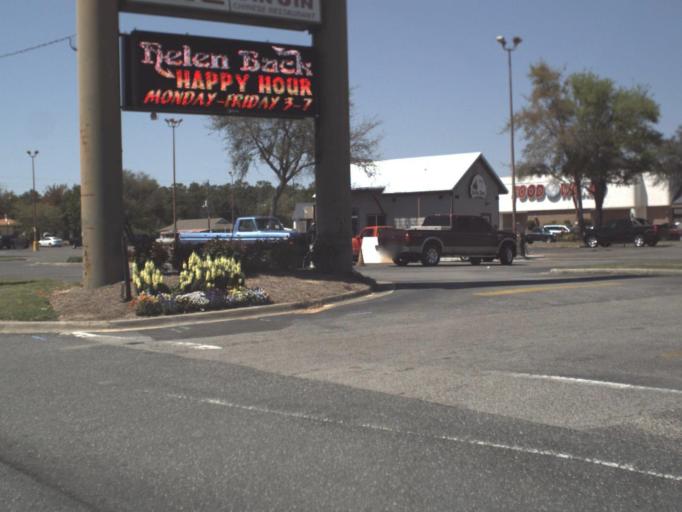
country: US
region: Florida
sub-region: Okaloosa County
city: Niceville
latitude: 30.5162
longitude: -86.4668
